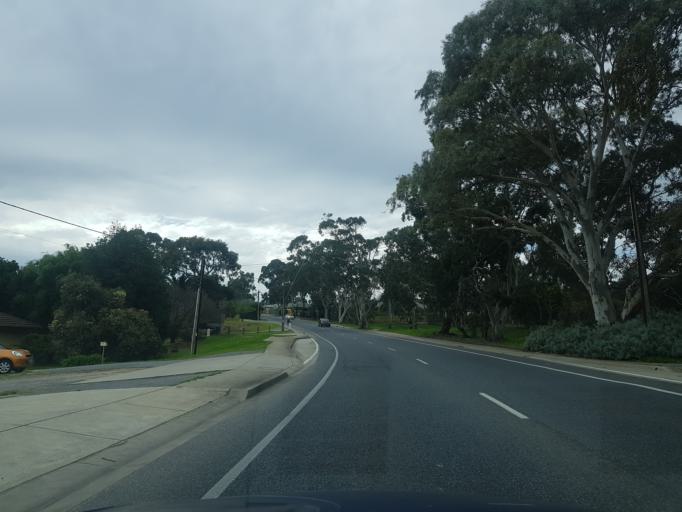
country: AU
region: South Australia
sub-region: Tea Tree Gully
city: Hope Valley
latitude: -34.8489
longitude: 138.7158
